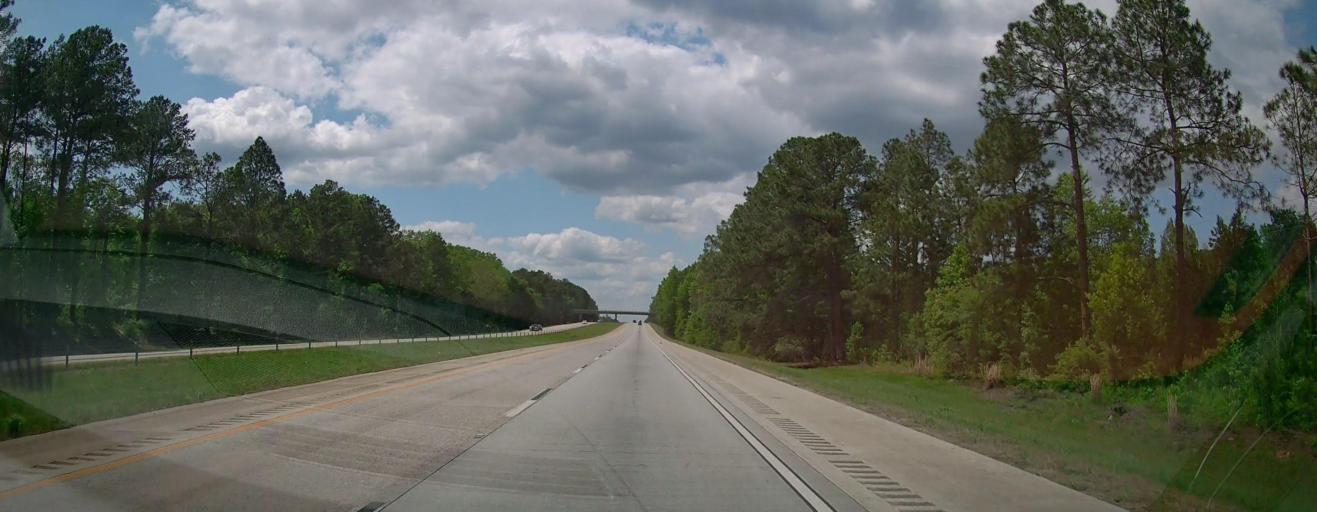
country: US
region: Georgia
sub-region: Treutlen County
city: Soperton
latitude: 32.4414
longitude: -82.7207
